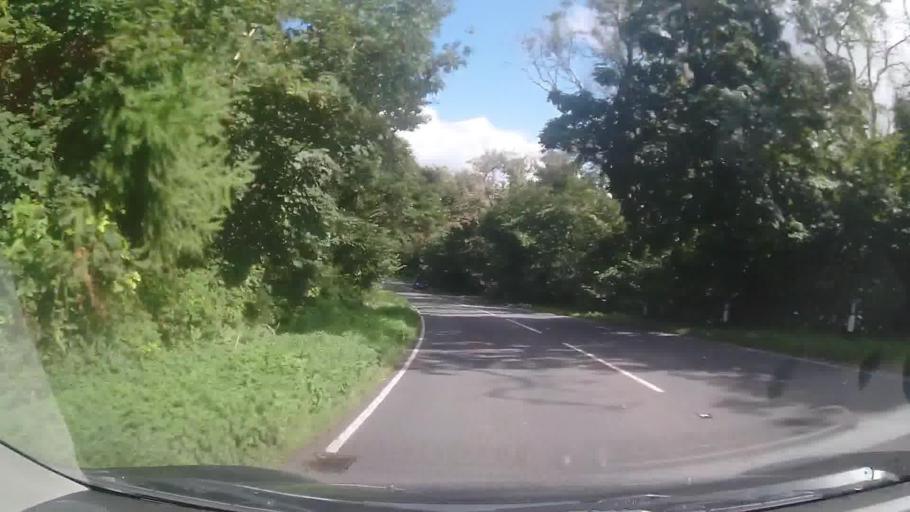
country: GB
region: Wales
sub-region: Pembrokeshire
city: Pembroke
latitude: 51.6837
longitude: -4.8813
